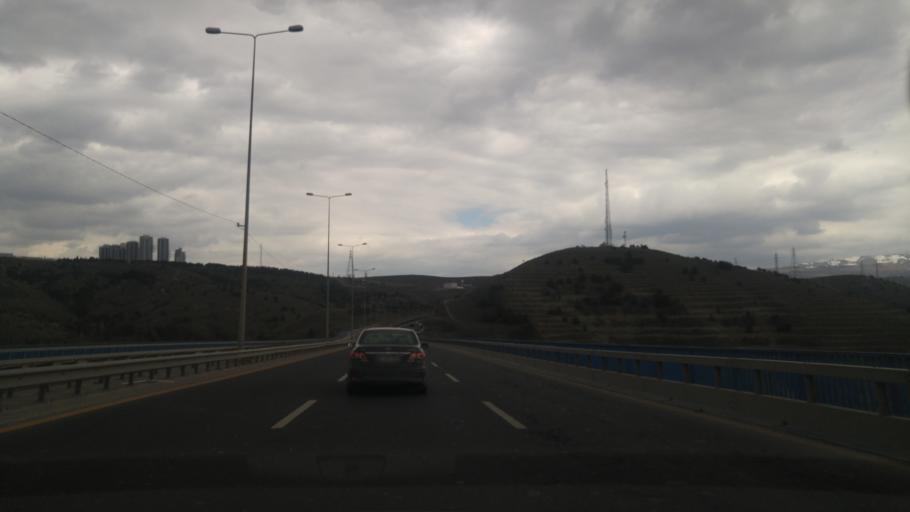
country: TR
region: Ankara
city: Mamak
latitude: 39.8891
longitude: 32.9077
